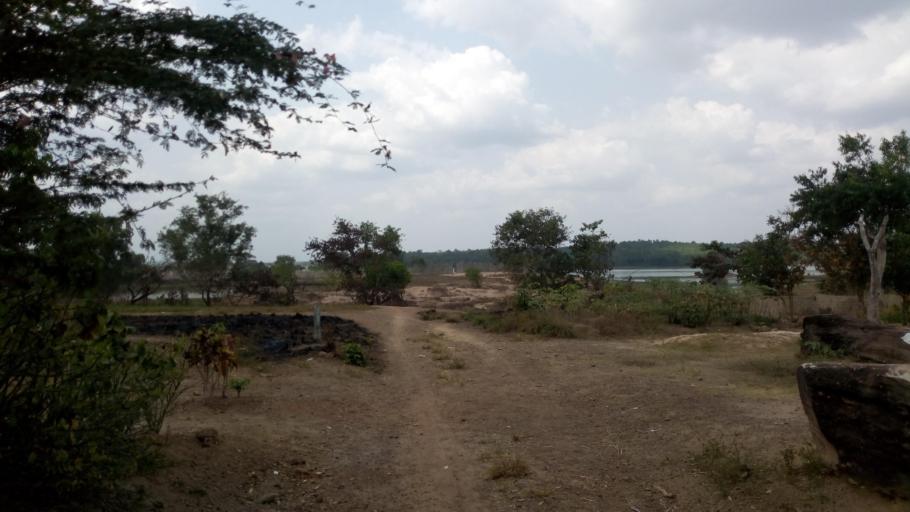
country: SL
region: Southern Province
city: Mogbwemo
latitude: 7.7947
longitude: -12.3043
